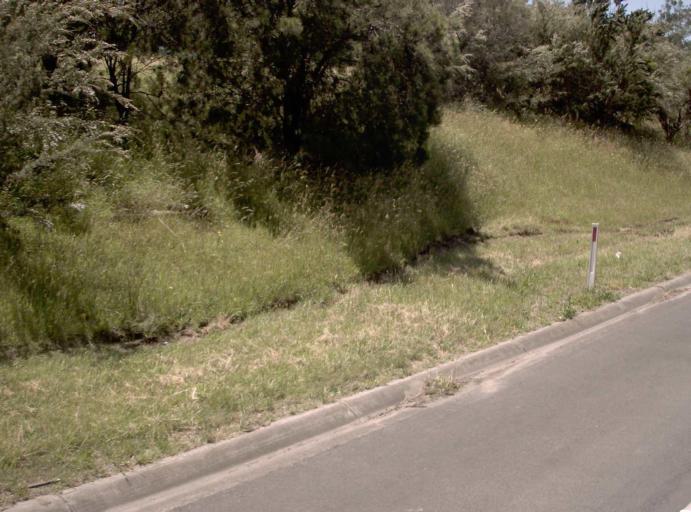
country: AU
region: Victoria
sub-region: Cardinia
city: Garfield
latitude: -38.0776
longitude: 145.6825
